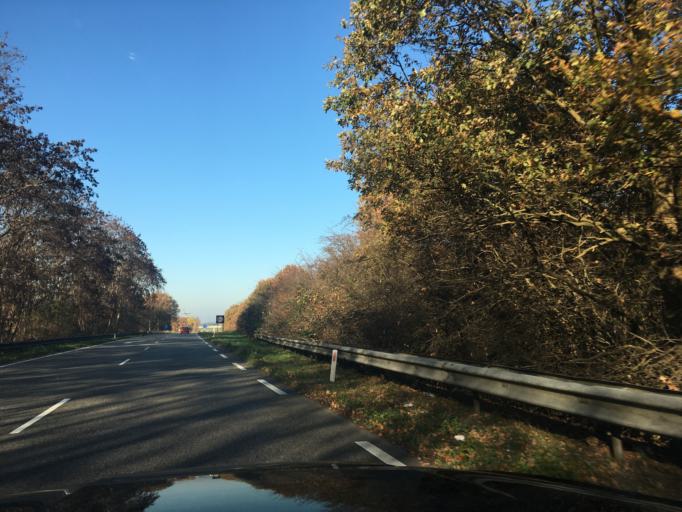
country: NL
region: North Brabant
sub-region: Gemeente Heusden
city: Heusden
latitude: 51.7005
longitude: 5.1644
